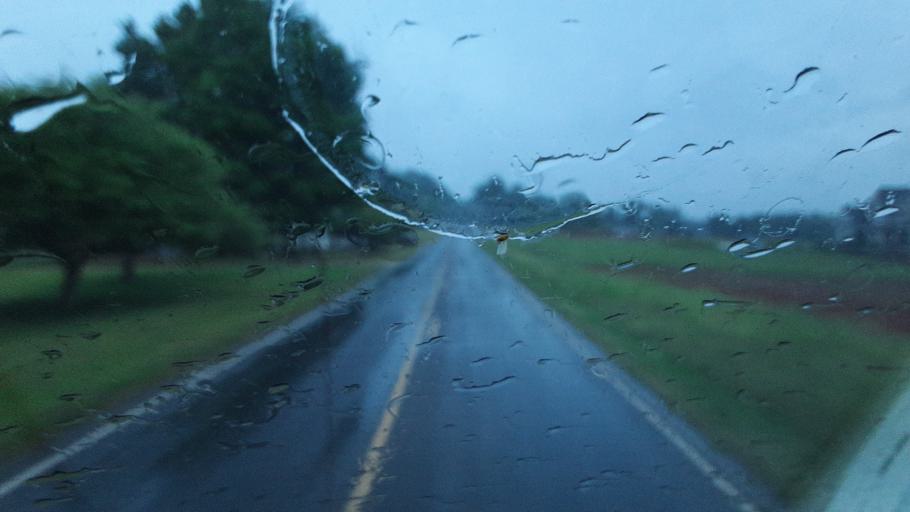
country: US
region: North Carolina
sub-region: Yadkin County
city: Jonesville
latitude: 36.0758
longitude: -80.8480
